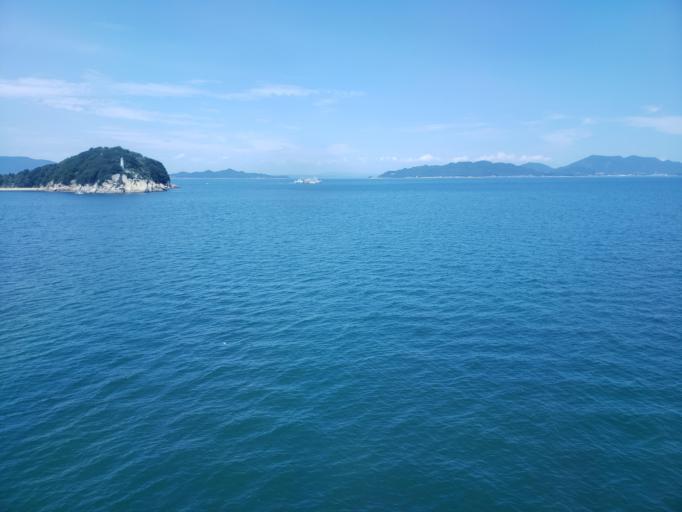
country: JP
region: Kagawa
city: Tonosho
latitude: 34.4055
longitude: 134.1401
